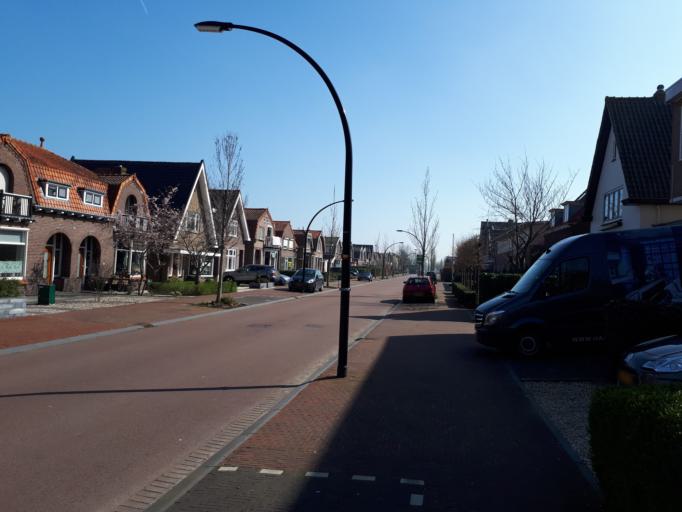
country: NL
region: South Holland
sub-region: Gemeente Krimpen aan den IJssel
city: Krimpen aan den IJssel
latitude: 51.9326
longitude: 4.6381
